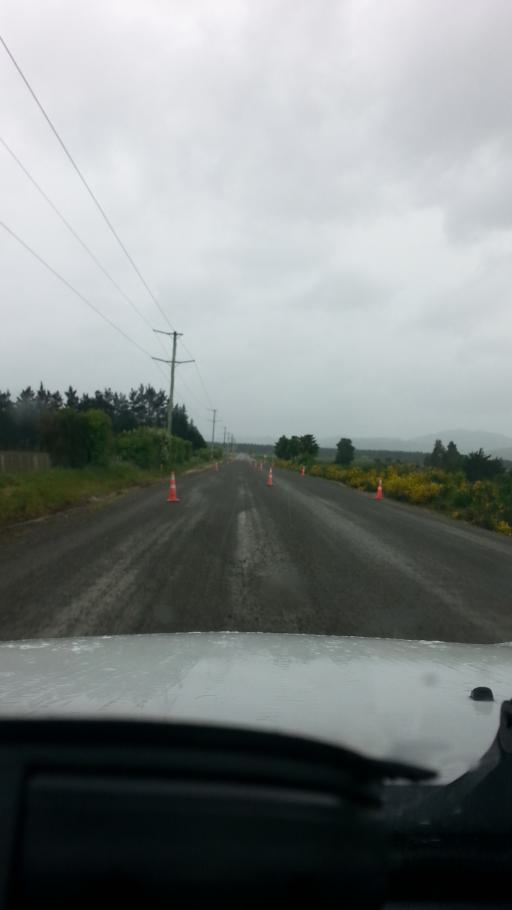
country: NZ
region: Wellington
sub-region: Masterton District
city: Masterton
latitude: -40.8232
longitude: 175.6245
